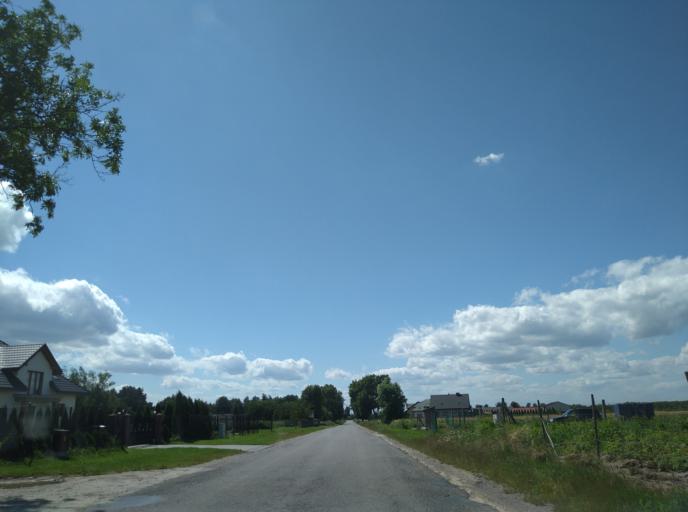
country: PL
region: Masovian Voivodeship
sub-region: Powiat grojecki
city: Goszczyn
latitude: 51.6680
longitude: 20.8753
